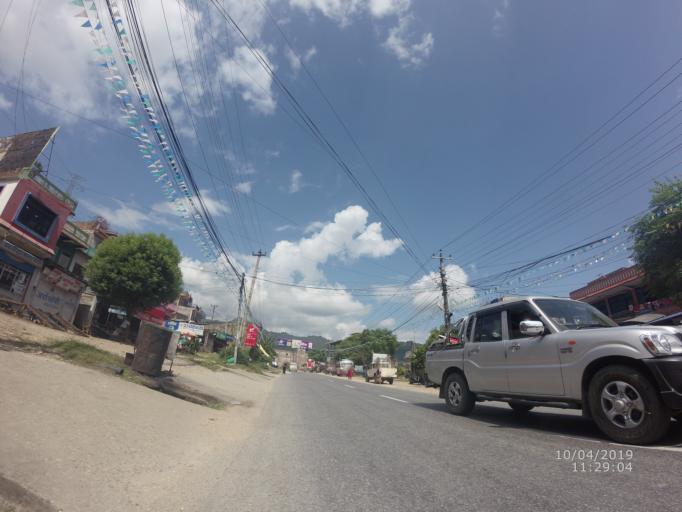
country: NP
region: Central Region
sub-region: Narayani Zone
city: Bharatpur
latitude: 27.9026
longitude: 84.5357
